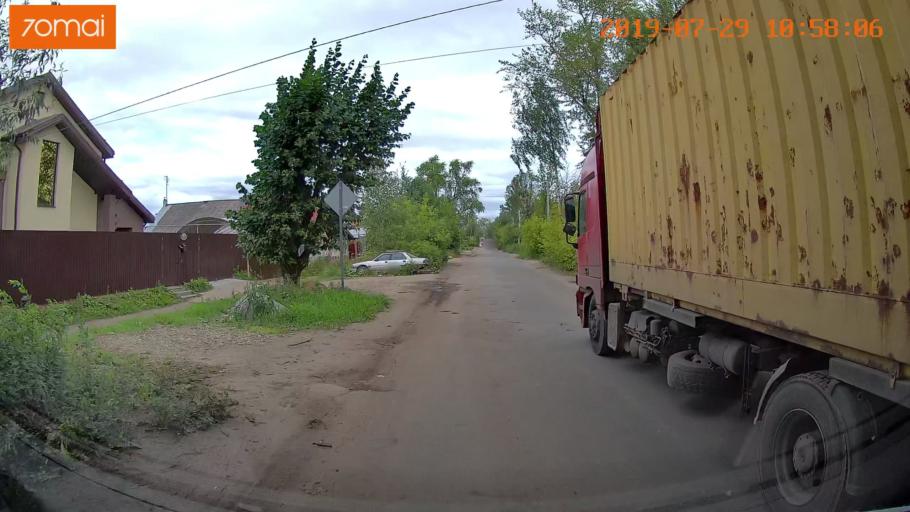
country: RU
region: Ivanovo
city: Bogorodskoye
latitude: 56.9922
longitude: 41.0376
